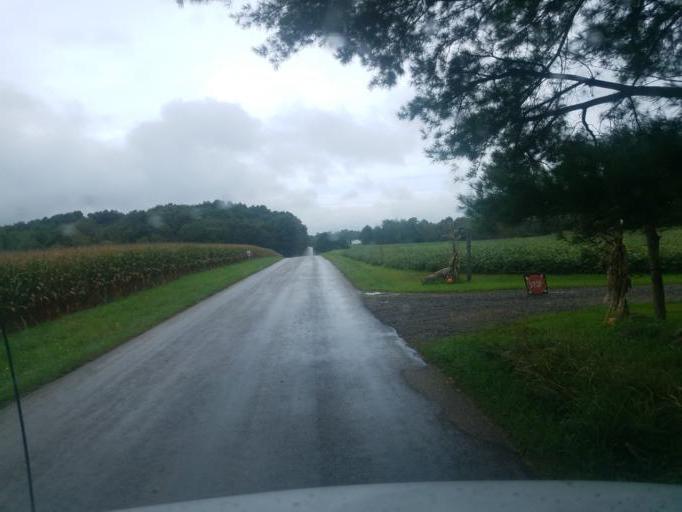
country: US
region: Ohio
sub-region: Wayne County
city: West Salem
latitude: 40.9559
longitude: -82.1114
